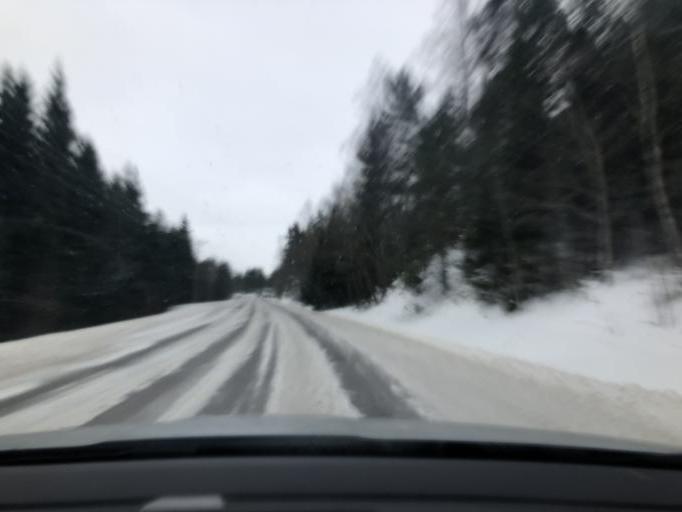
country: SE
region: OEstergoetland
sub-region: Kinda Kommun
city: Kisa
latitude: 58.0224
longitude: 15.7645
